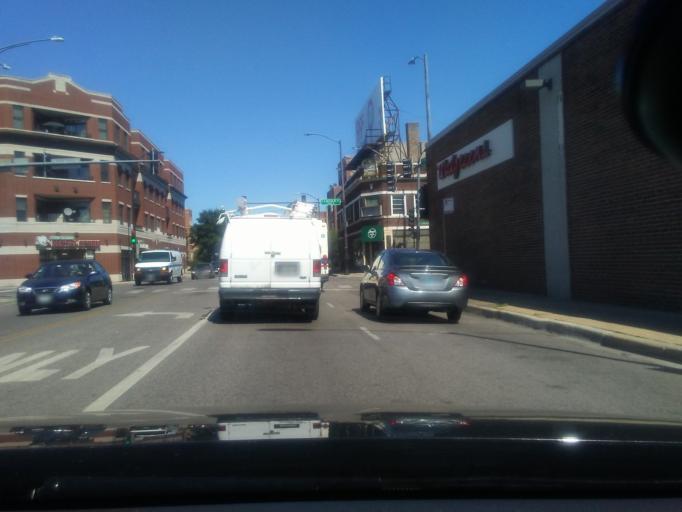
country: US
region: Illinois
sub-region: Cook County
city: Lincolnwood
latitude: 41.9758
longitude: -87.6928
